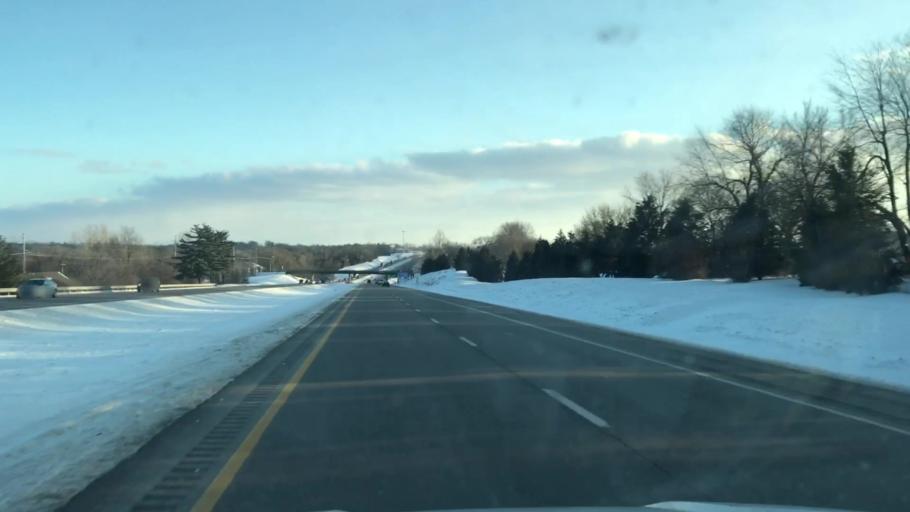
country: US
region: Missouri
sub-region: Andrew County
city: Country Club Village
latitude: 39.7961
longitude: -94.7977
